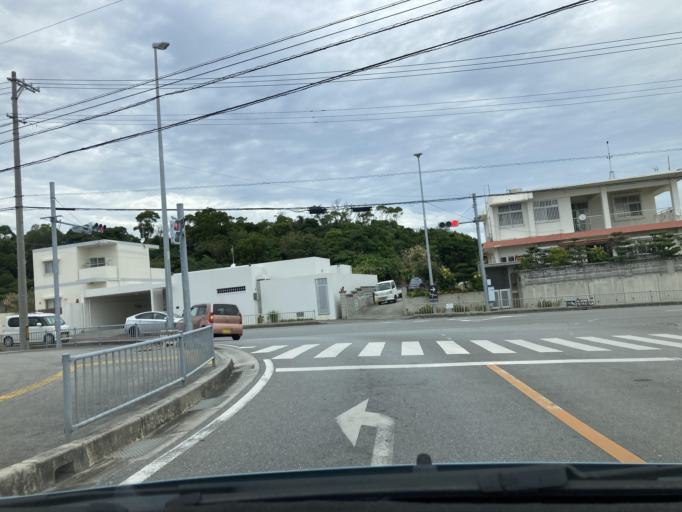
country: JP
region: Okinawa
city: Ishikawa
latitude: 26.4024
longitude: 127.7392
